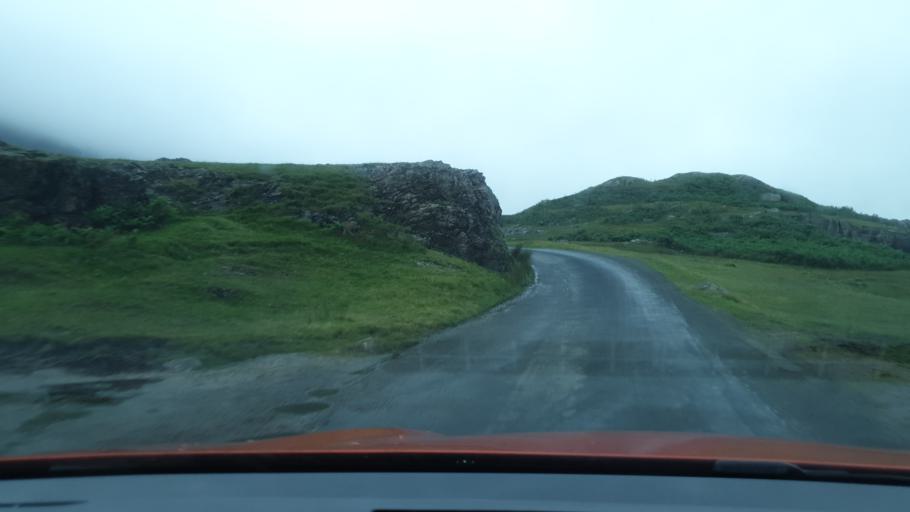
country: GB
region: England
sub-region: Cumbria
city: Seascale
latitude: 54.4363
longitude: -3.3114
